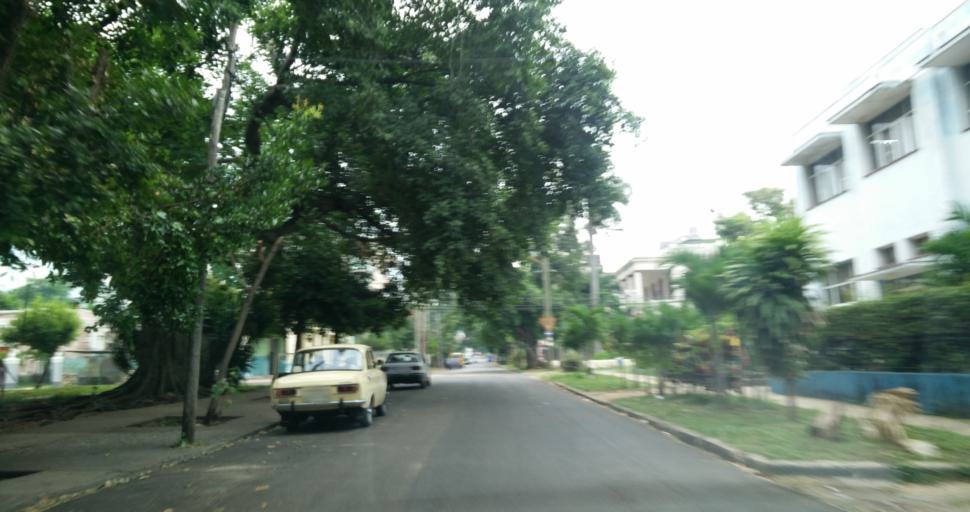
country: CU
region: La Habana
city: Havana
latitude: 23.1384
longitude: -82.3882
